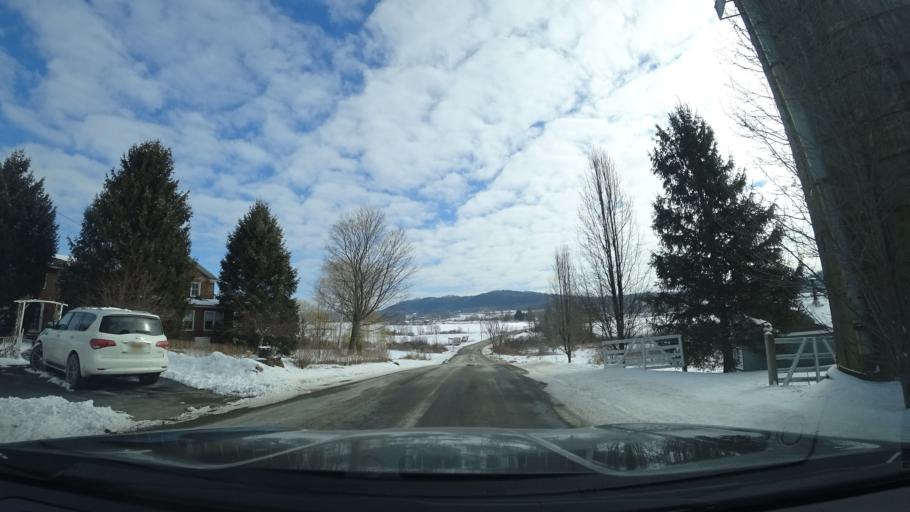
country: US
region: New York
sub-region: Washington County
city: Fort Edward
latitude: 43.2533
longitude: -73.4801
